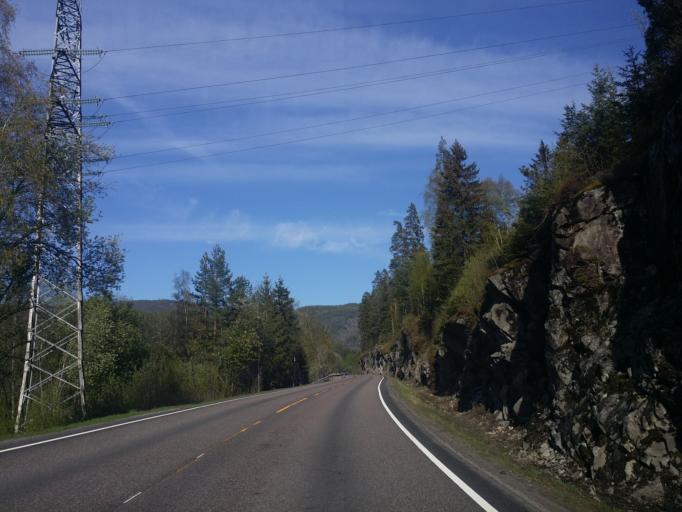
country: NO
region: Telemark
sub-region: Hjartdal
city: Sauland
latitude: 59.6104
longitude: 8.9811
